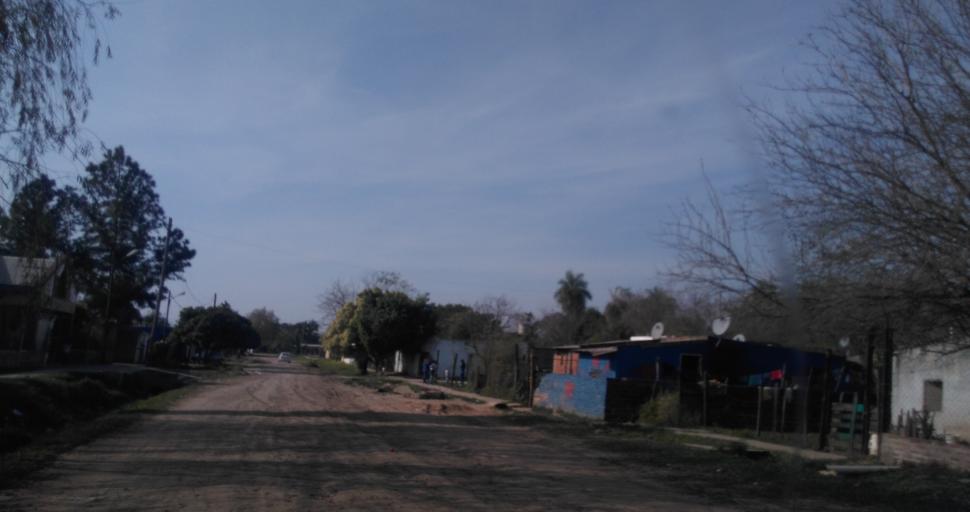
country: AR
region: Chaco
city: Fontana
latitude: -27.4294
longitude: -59.0179
